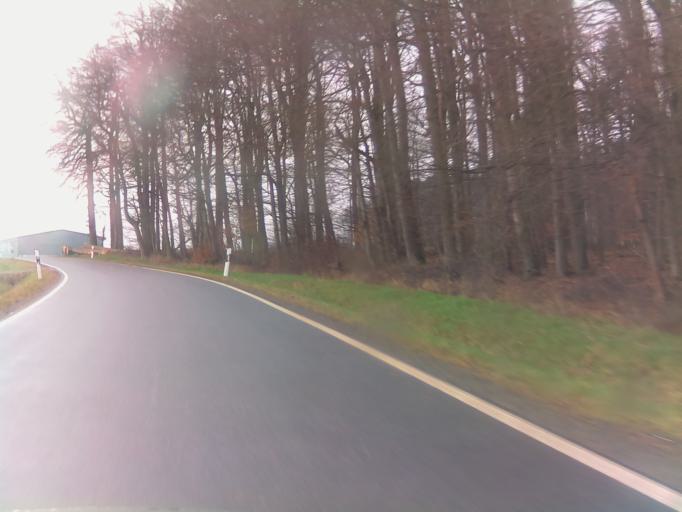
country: DE
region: Rheinland-Pfalz
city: Gosenroth
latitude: 49.8956
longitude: 7.3266
